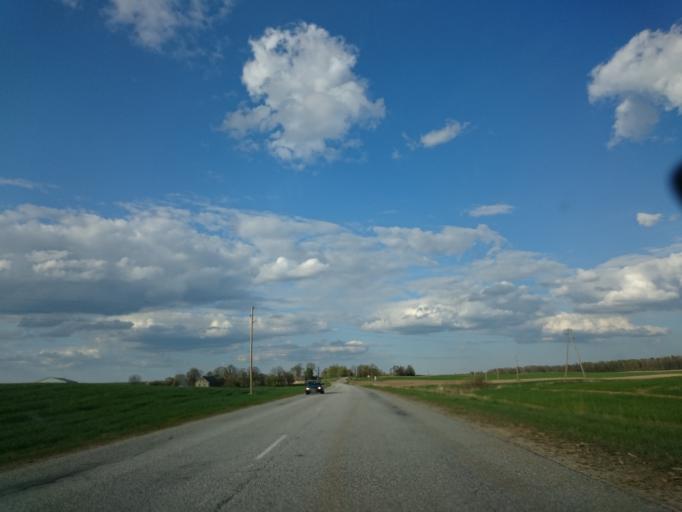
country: LV
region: Aizpute
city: Aizpute
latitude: 56.8250
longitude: 21.7393
